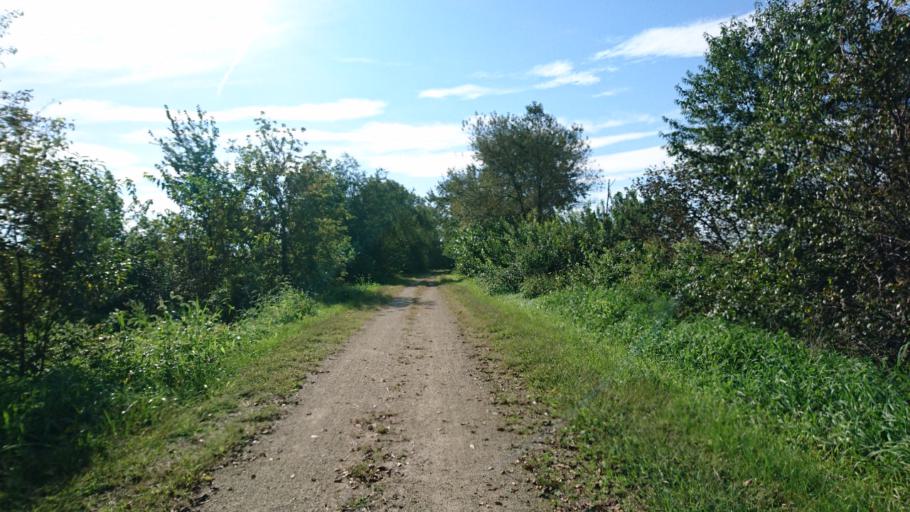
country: US
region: Illinois
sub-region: Will County
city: Manhattan
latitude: 41.4659
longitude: -88.0201
